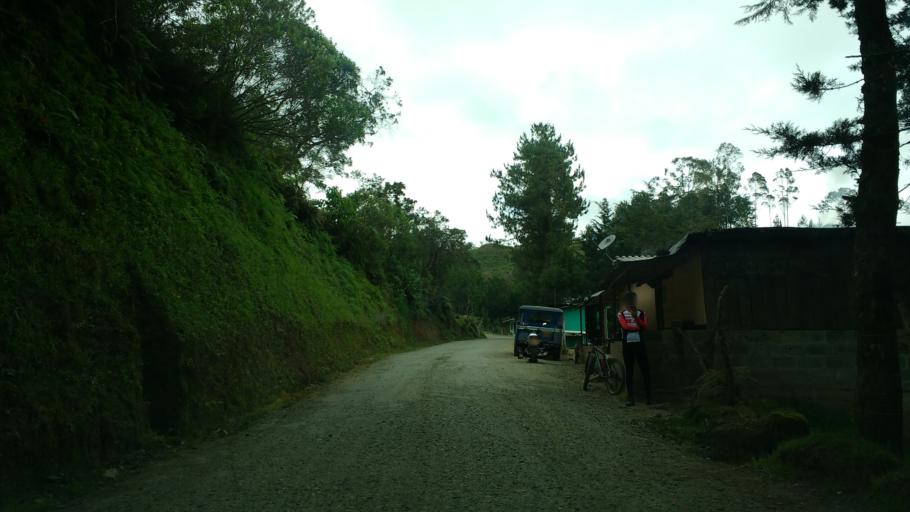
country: CO
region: Antioquia
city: Concepcion
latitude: 6.3443
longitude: -75.2684
